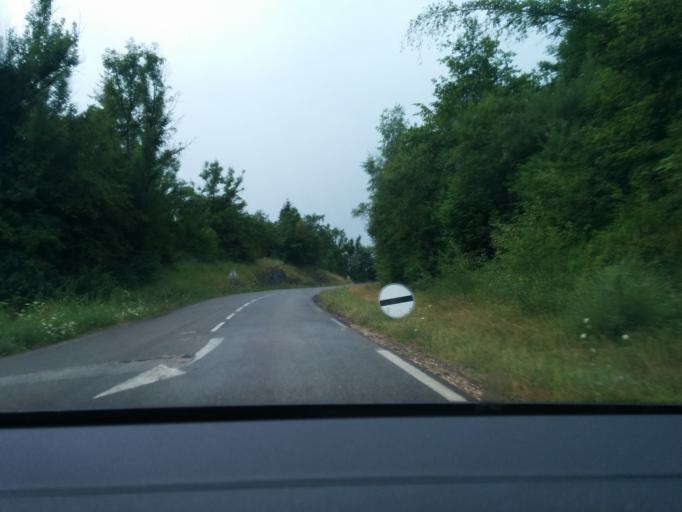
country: FR
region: Franche-Comte
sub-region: Departement du Jura
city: Saint-Lupicin
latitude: 46.4208
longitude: 5.8026
